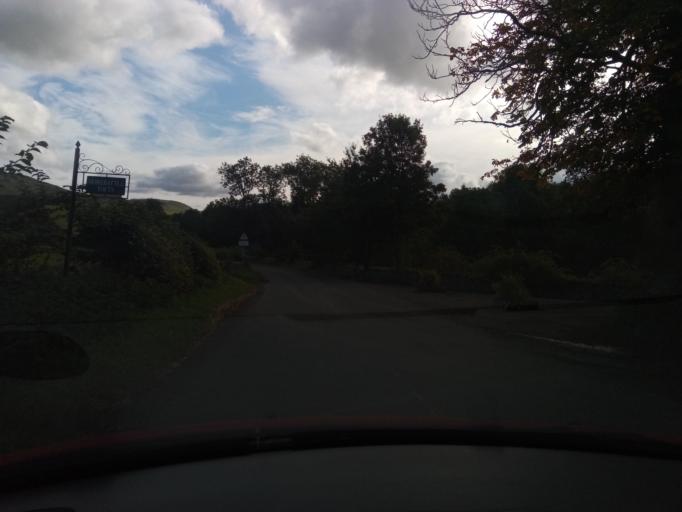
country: GB
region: Scotland
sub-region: The Scottish Borders
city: Kelso
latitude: 55.5222
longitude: -2.3558
